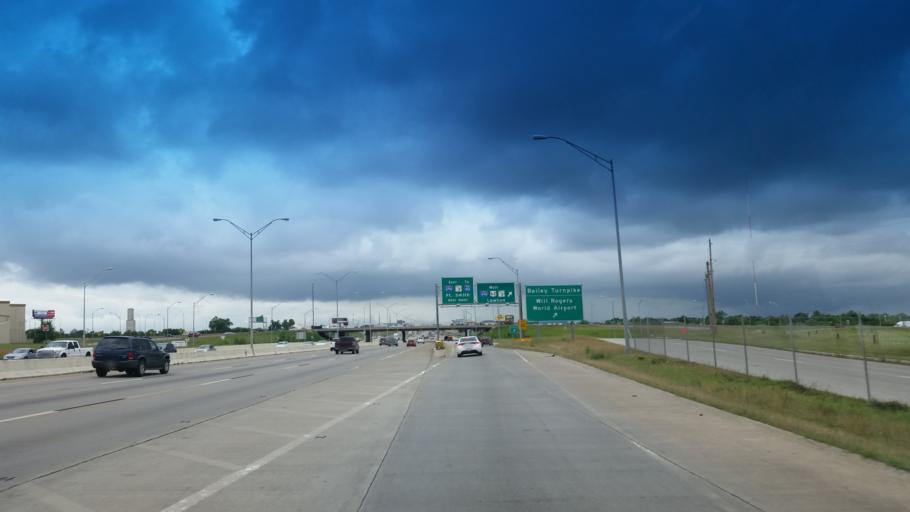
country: US
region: Oklahoma
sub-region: Cleveland County
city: Moore
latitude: 35.3950
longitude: -97.4953
